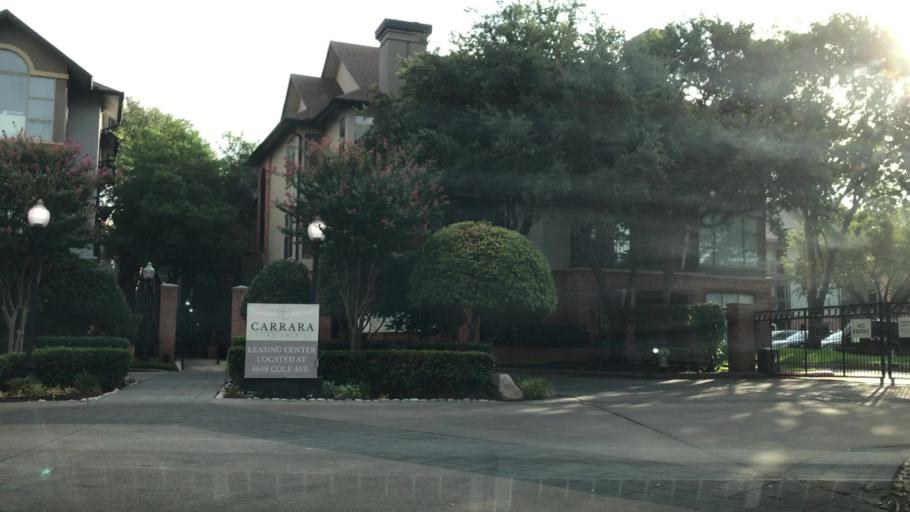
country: US
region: Texas
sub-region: Dallas County
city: Highland Park
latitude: 32.8243
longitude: -96.7899
